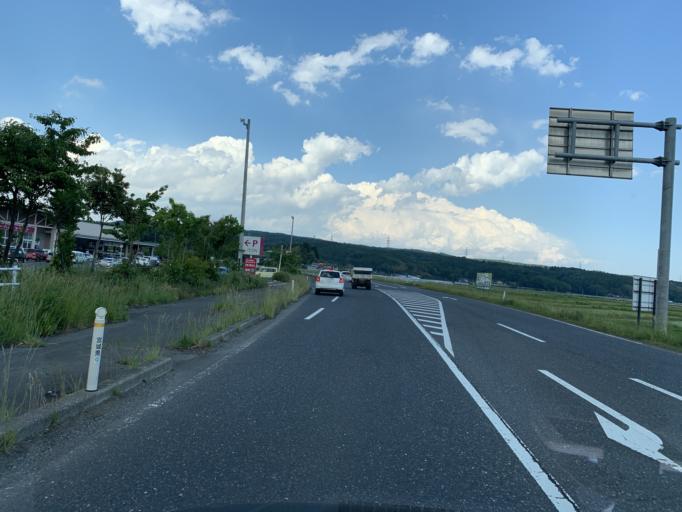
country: JP
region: Miyagi
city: Wakuya
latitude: 38.5357
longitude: 141.1481
